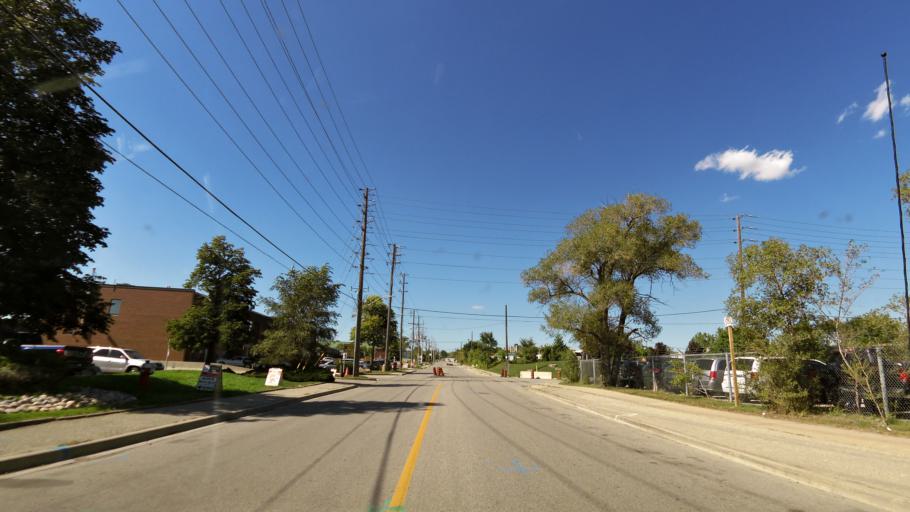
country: CA
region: Ontario
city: Etobicoke
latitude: 43.5931
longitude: -79.5906
